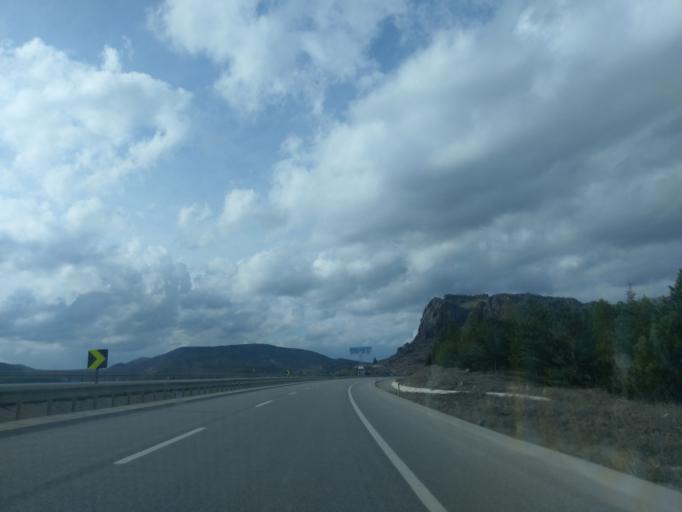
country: TR
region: Kuetahya
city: Sabuncu
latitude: 39.5711
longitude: 30.1066
